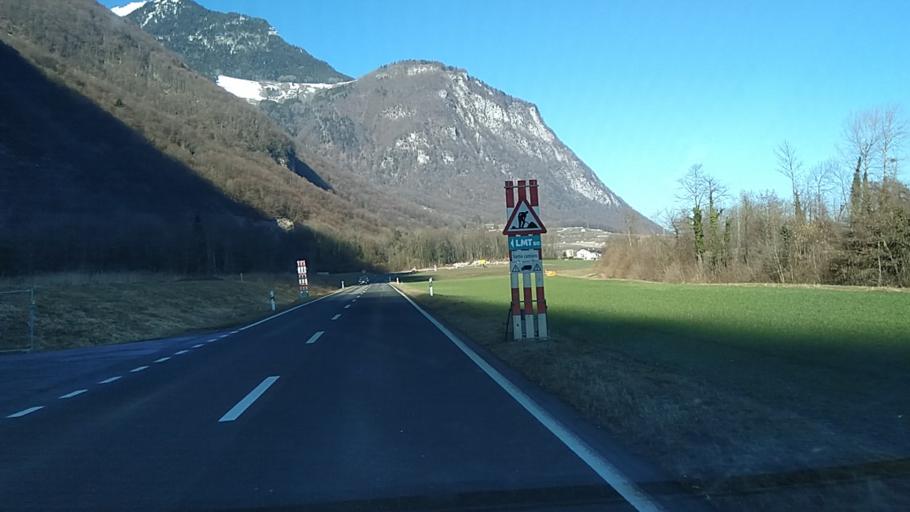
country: CH
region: Valais
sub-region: Monthey District
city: Vouvry
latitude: 46.3506
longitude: 6.8837
